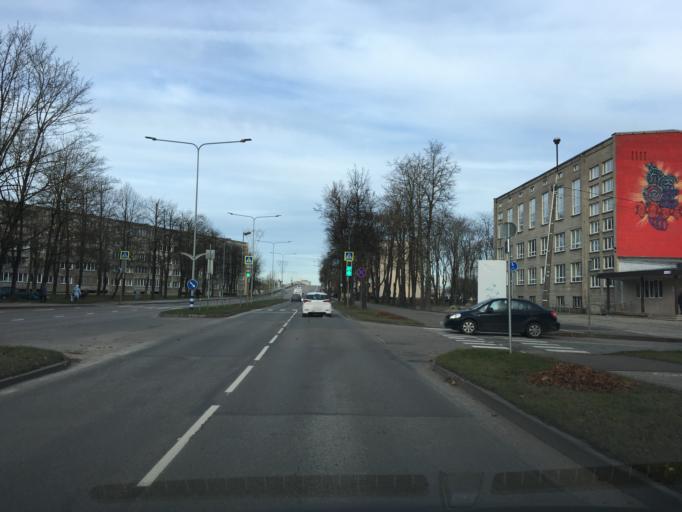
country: EE
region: Ida-Virumaa
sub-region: Narva linn
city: Narva
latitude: 59.3682
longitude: 28.1862
